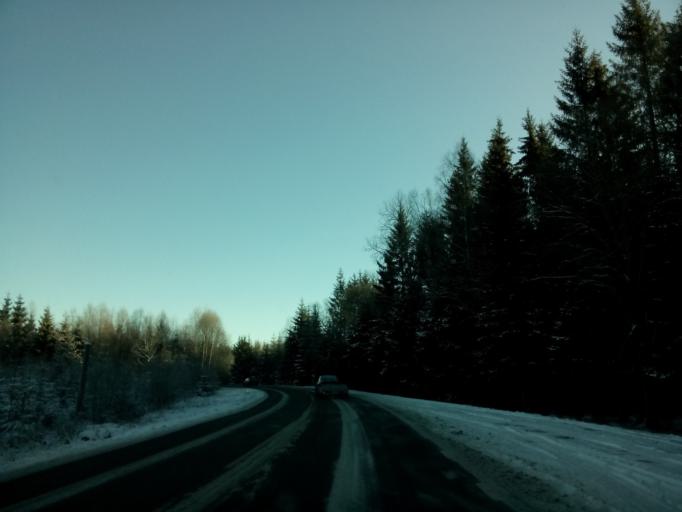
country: SE
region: Vaestra Goetaland
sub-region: Vargarda Kommun
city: Vargarda
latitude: 57.9908
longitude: 12.9056
